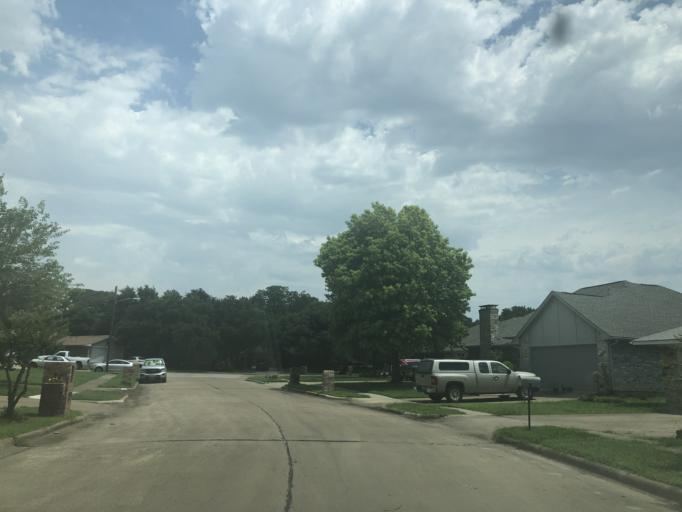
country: US
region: Texas
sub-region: Dallas County
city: Irving
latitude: 32.7893
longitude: -96.9381
